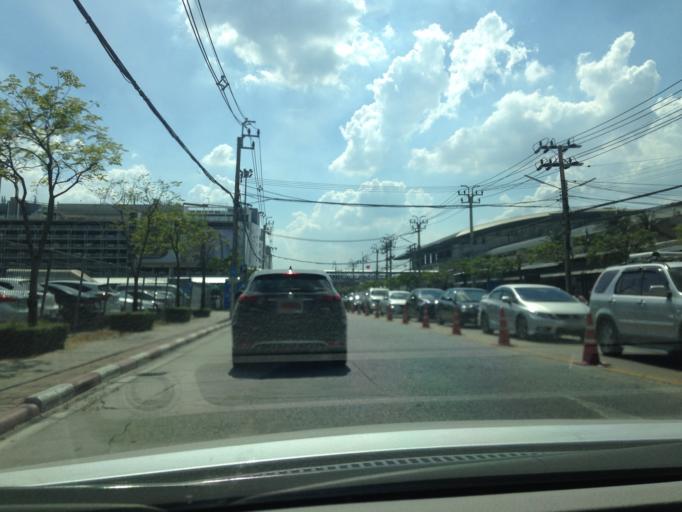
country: TH
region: Bangkok
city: Lak Si
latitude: 13.9137
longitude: 100.5504
